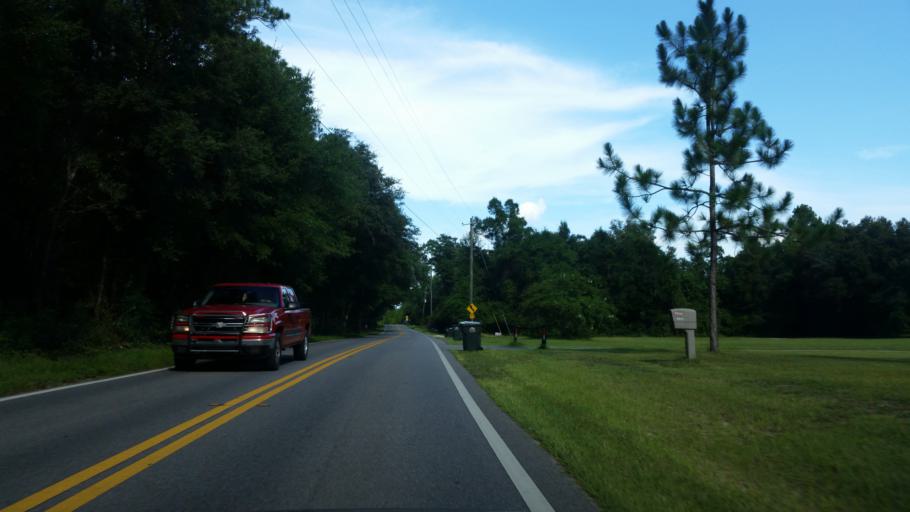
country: US
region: Florida
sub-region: Santa Rosa County
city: Pace
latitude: 30.6248
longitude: -87.1130
